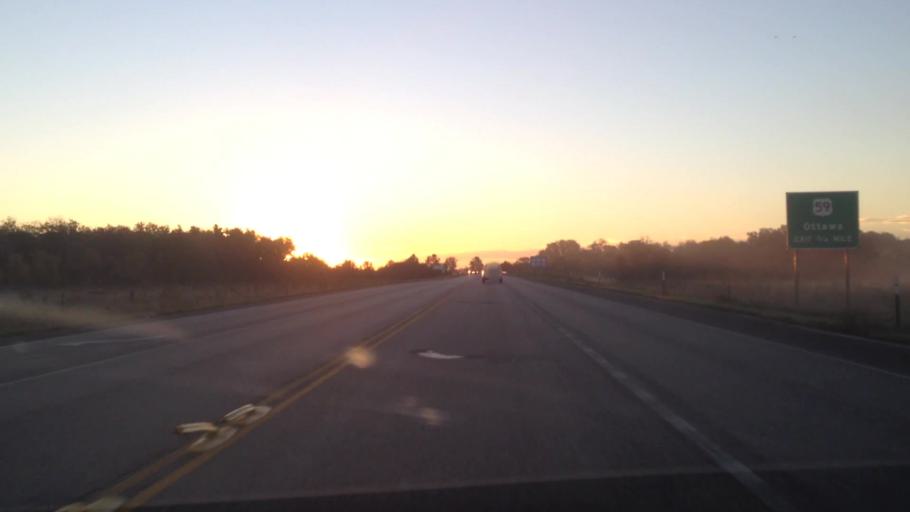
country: US
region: Kansas
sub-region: Douglas County
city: Lawrence
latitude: 38.9223
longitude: -95.2784
